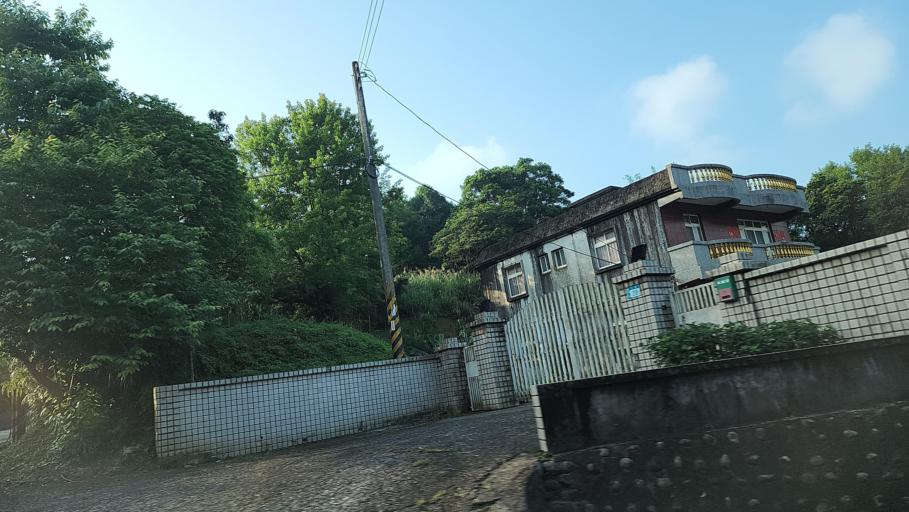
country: TW
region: Taiwan
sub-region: Keelung
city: Keelung
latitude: 25.1751
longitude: 121.6532
